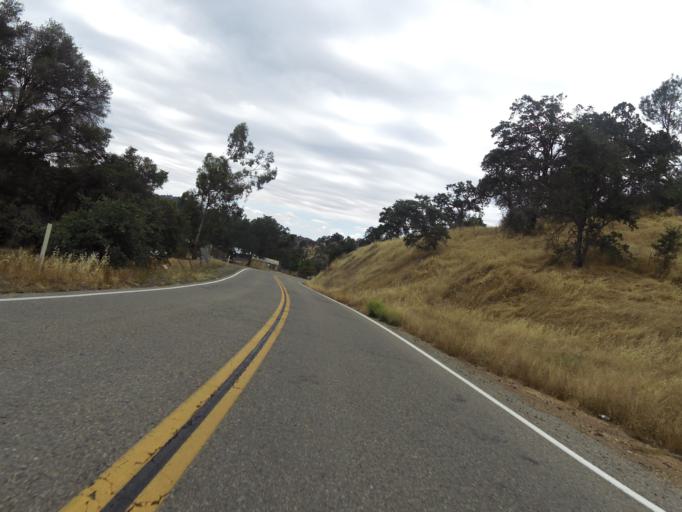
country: US
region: California
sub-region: Madera County
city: Coarsegold
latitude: 37.2391
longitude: -119.7402
